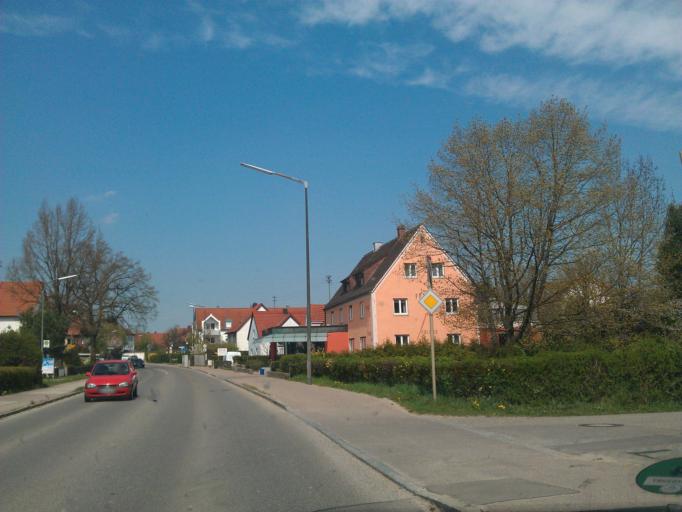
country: DE
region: Bavaria
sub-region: Swabia
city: Aichach
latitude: 48.4671
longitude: 11.1251
